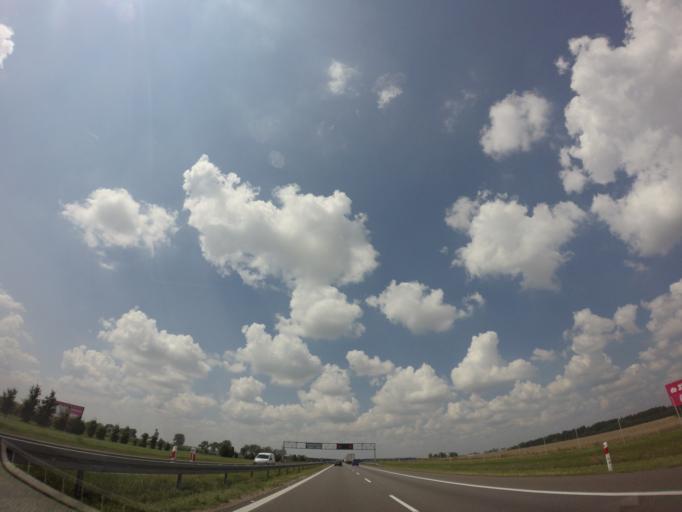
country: PL
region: Opole Voivodeship
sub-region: Powiat strzelecki
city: Ujazd
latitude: 50.4485
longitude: 18.3309
